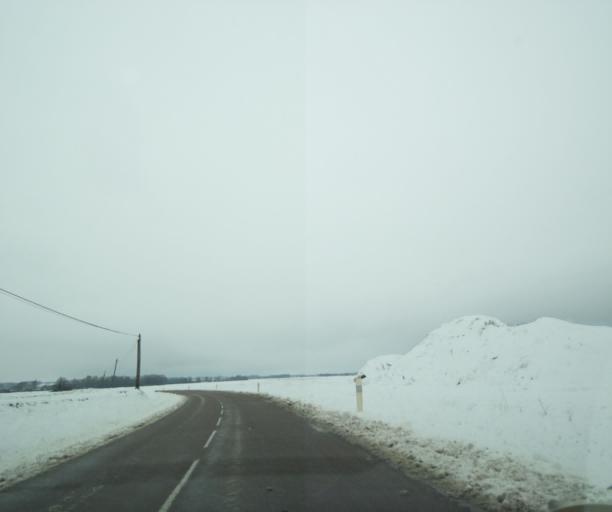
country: FR
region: Champagne-Ardenne
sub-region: Departement de la Haute-Marne
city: Montier-en-Der
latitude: 48.4475
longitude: 4.7995
